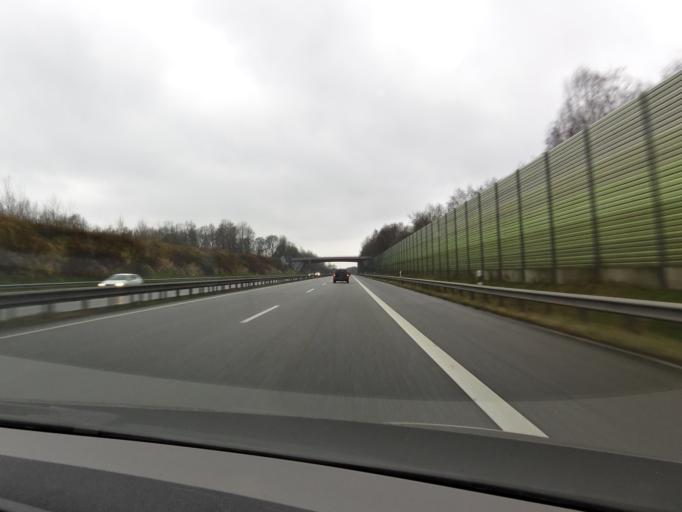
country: DE
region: Schleswig-Holstein
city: Glinde
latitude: 53.5576
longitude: 10.2139
